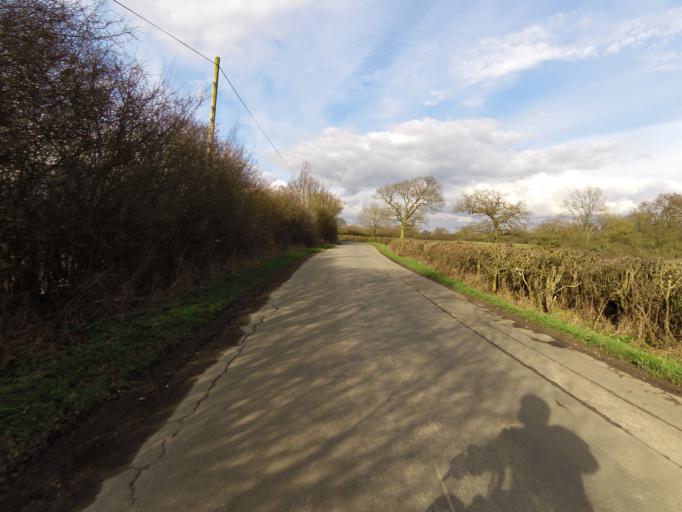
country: GB
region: England
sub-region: Doncaster
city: Stainforth
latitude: 53.6391
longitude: -1.0325
